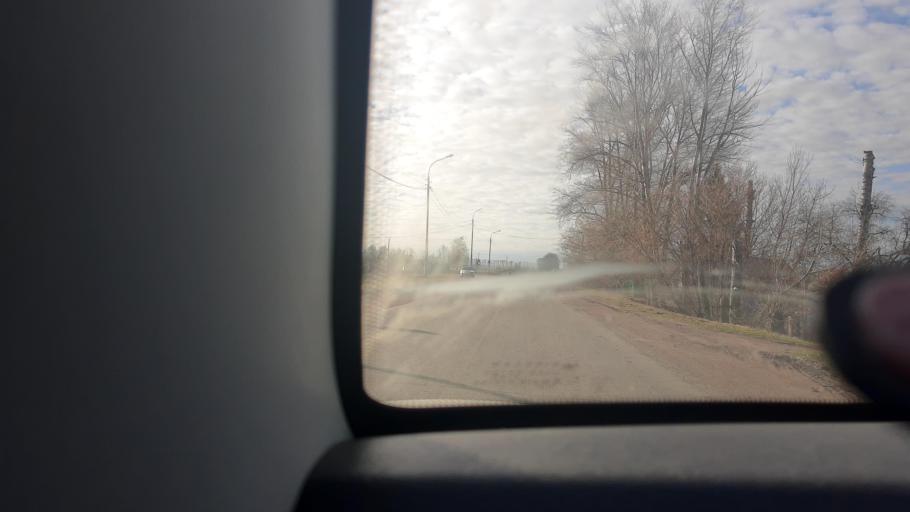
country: RU
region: Bashkortostan
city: Asanovo
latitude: 54.9583
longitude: 55.5520
